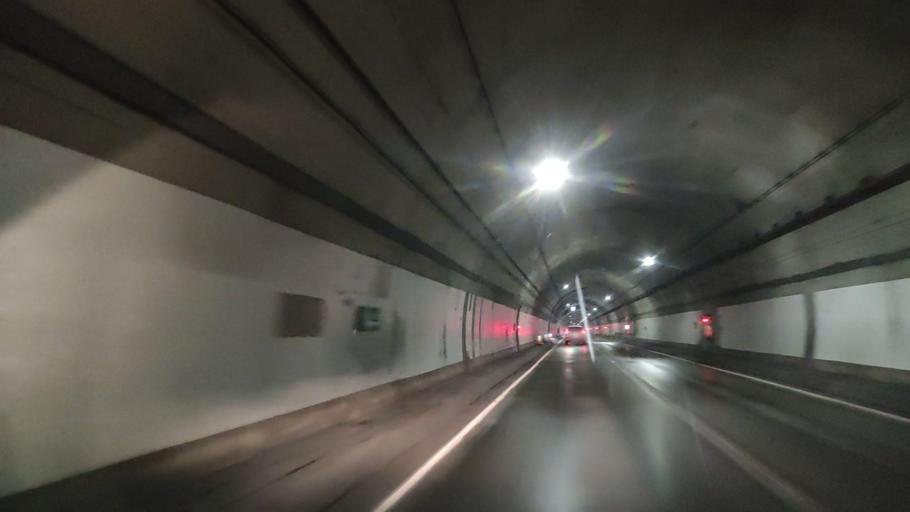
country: JP
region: Hokkaido
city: Rumoi
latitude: 43.7061
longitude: 141.3347
